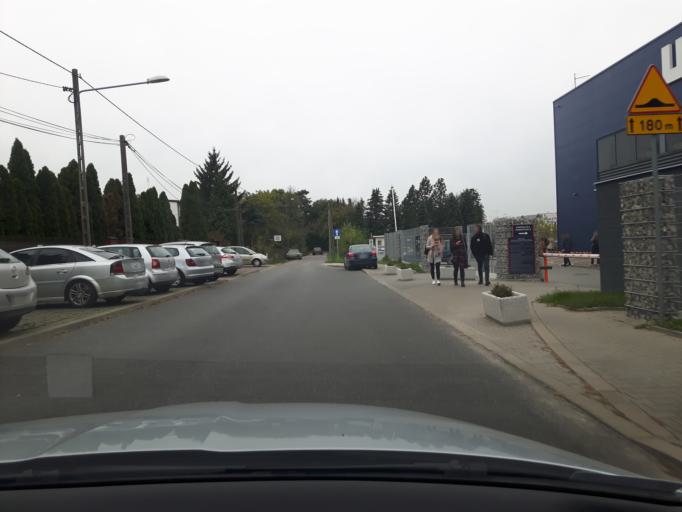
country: PL
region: Masovian Voivodeship
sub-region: Warszawa
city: Wlochy
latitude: 52.1976
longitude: 20.9326
